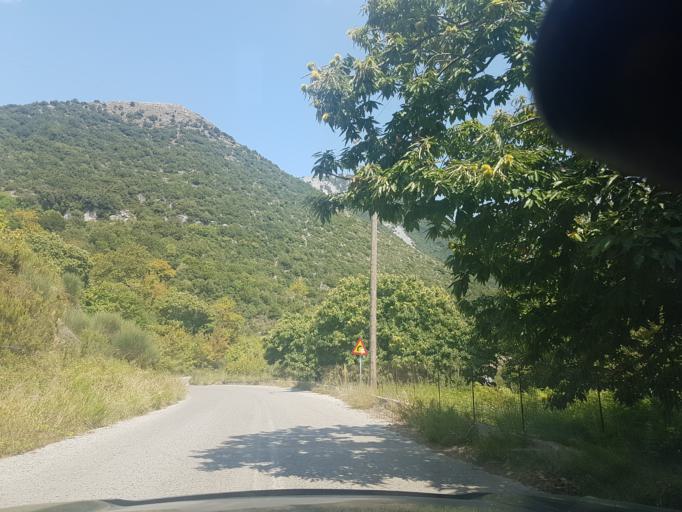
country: GR
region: Central Greece
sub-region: Nomos Evvoias
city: Kymi
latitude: 38.6456
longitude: 23.8998
